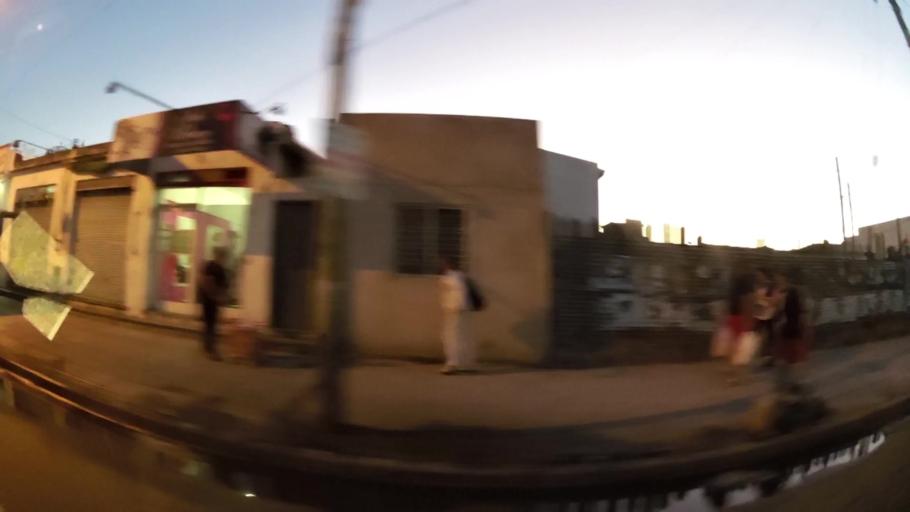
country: AR
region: Buenos Aires
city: San Justo
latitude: -34.7129
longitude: -58.5932
